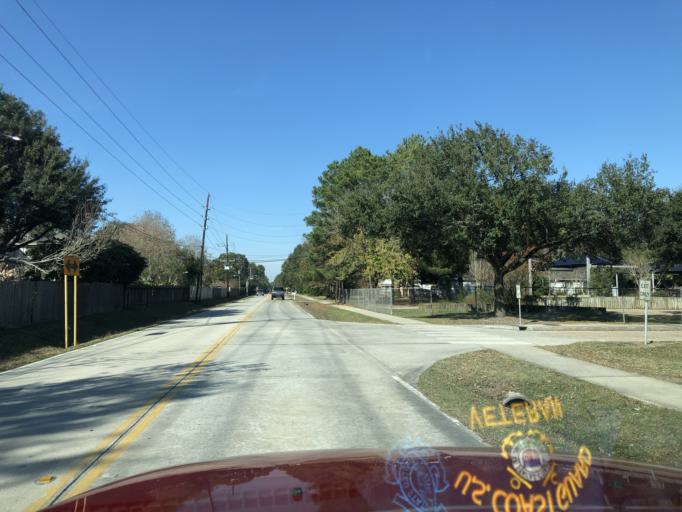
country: US
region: Texas
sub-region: Harris County
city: Tomball
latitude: 30.0248
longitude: -95.5410
